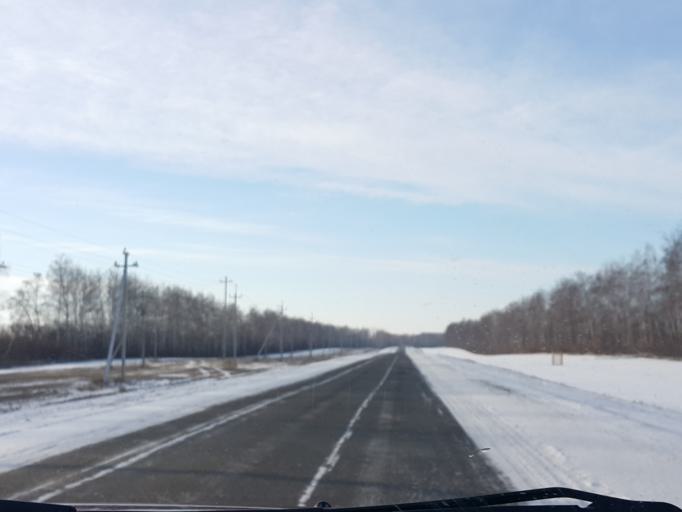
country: RU
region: Tambov
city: Znamenka
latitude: 52.3867
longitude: 41.3409
